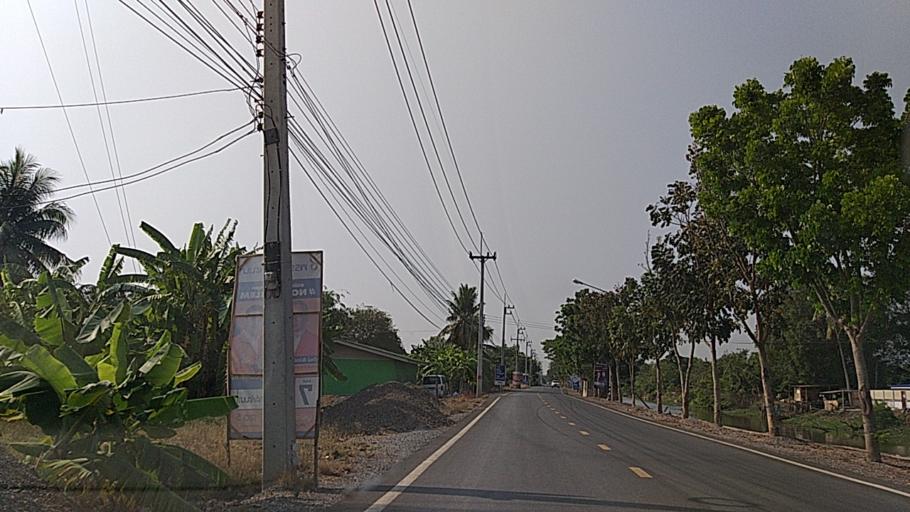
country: TH
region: Pathum Thani
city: Thanyaburi
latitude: 13.9833
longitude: 100.7059
